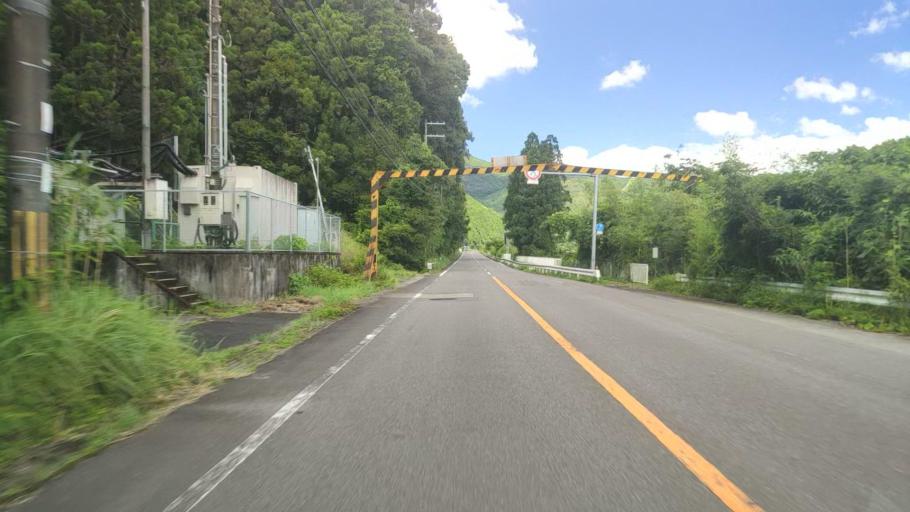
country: JP
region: Wakayama
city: Shingu
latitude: 33.8085
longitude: 135.8685
